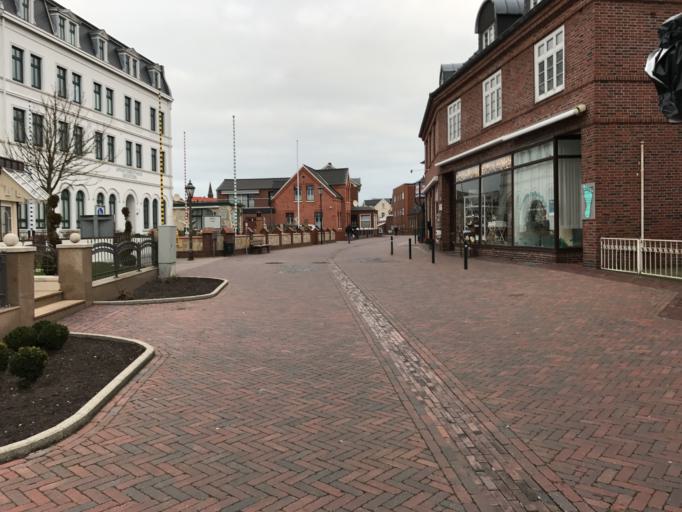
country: DE
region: Lower Saxony
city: Borkum
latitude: 53.5853
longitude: 6.6654
